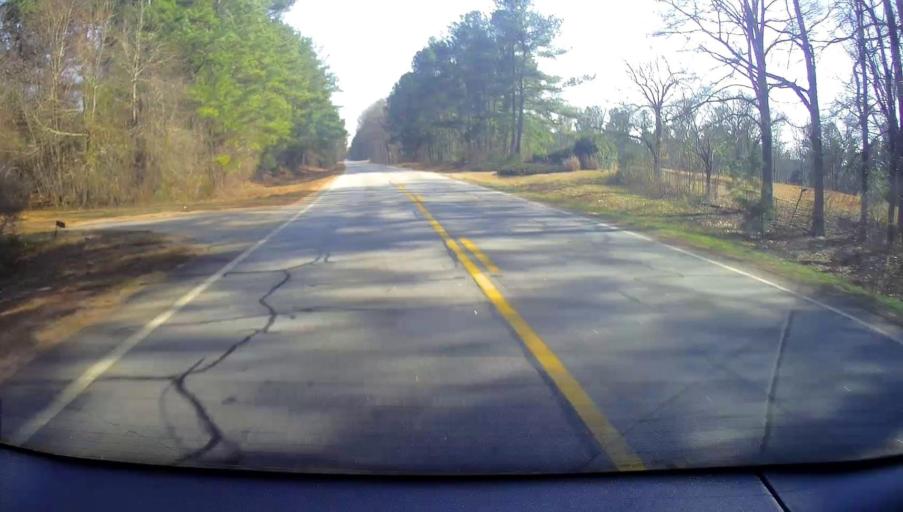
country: US
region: Georgia
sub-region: Butts County
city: Indian Springs
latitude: 33.2276
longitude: -83.8743
